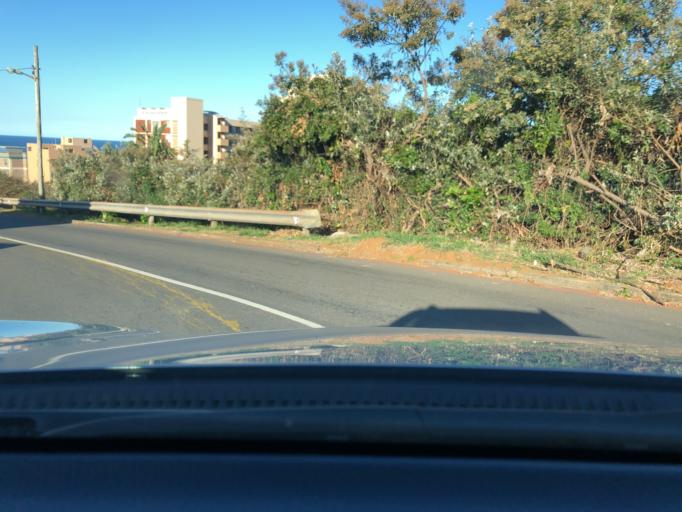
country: ZA
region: KwaZulu-Natal
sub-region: eThekwini Metropolitan Municipality
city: Umkomaas
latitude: -30.0457
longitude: 30.8911
